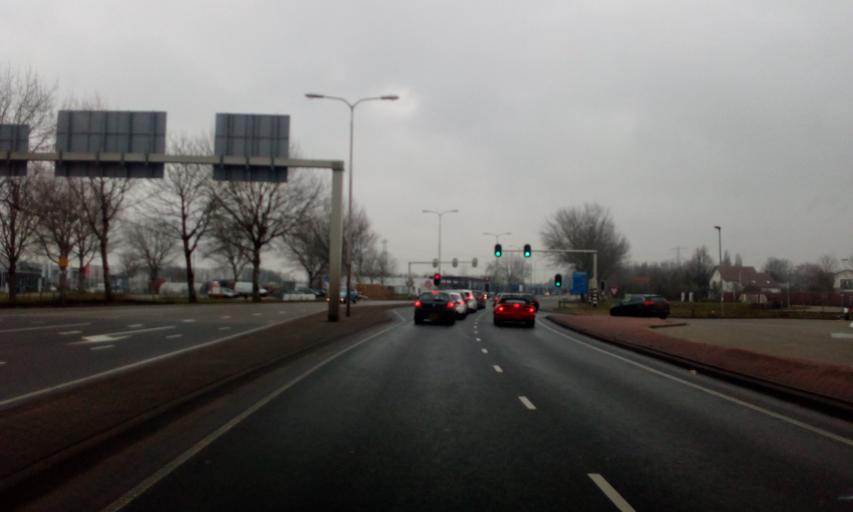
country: NL
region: Utrecht
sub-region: Gemeente Woerden
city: Woerden
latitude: 52.0758
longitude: 4.9017
